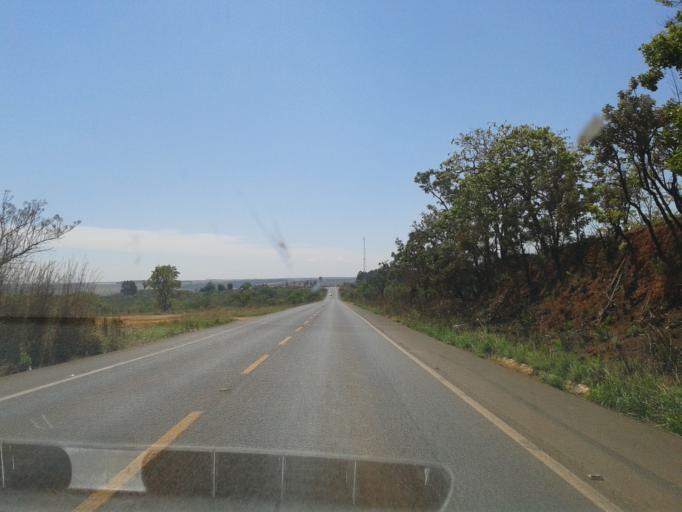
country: BR
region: Minas Gerais
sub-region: Sacramento
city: Sacramento
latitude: -19.3215
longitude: -47.5561
